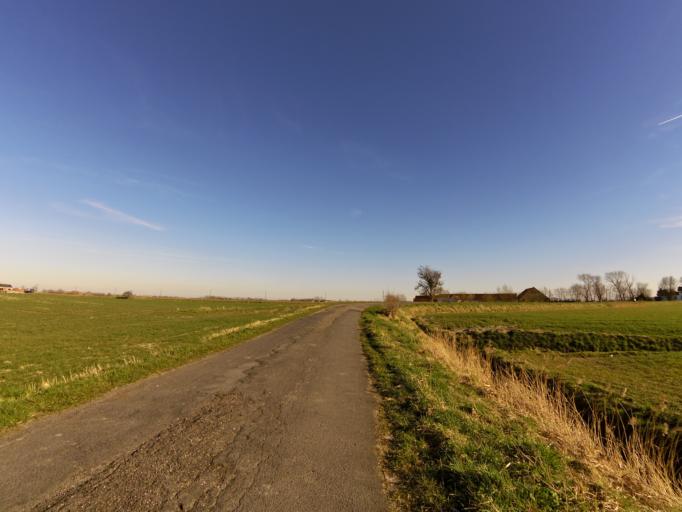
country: BE
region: Flanders
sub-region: Provincie West-Vlaanderen
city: Ostend
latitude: 51.1966
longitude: 2.9299
